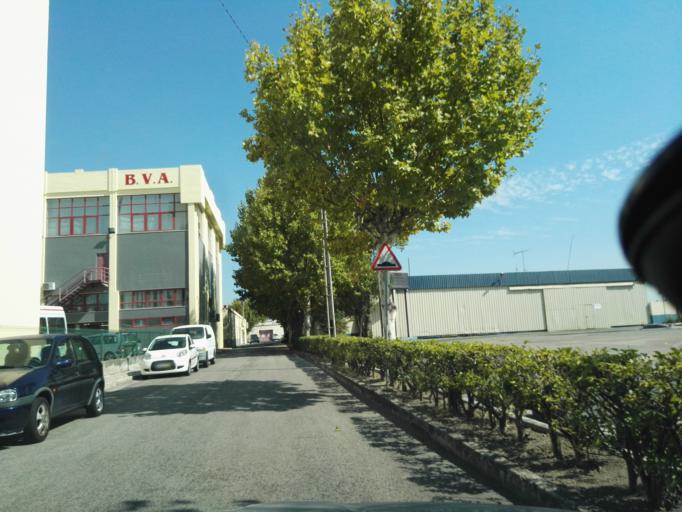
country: PT
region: Lisbon
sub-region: Vila Franca de Xira
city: Alhandra
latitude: 38.9253
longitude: -9.0081
